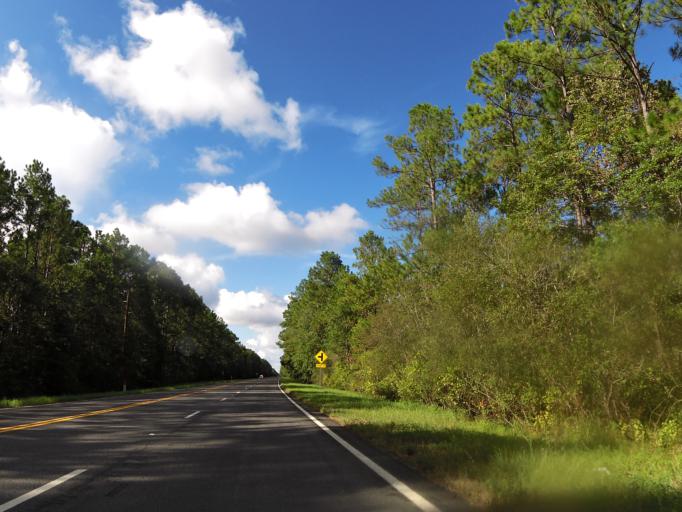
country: US
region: Georgia
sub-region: Camden County
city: Woodbine
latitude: 31.0042
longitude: -81.7319
